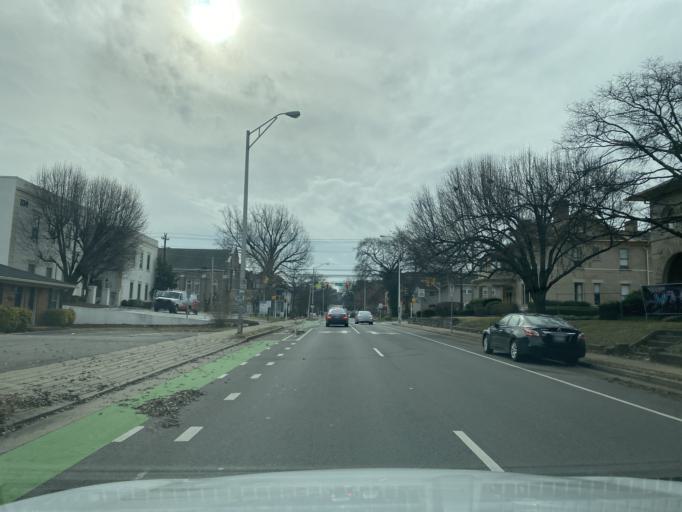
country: US
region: Tennessee
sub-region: Davidson County
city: Nashville
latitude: 36.1442
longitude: -86.7943
